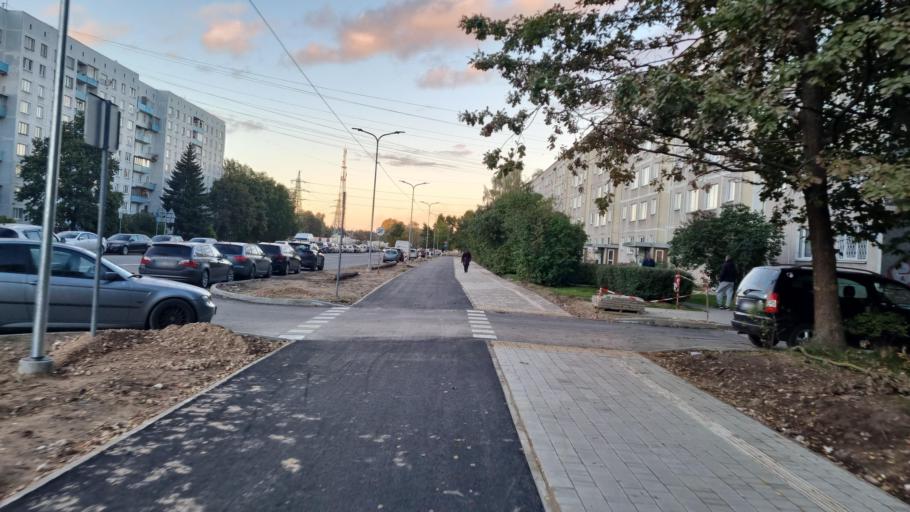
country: LV
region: Marupe
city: Marupe
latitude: 56.9633
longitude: 24.0242
